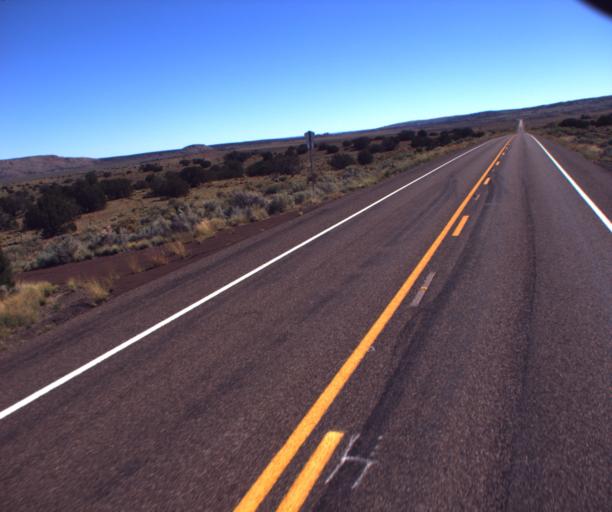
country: US
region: Arizona
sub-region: Apache County
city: Saint Johns
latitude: 34.5951
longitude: -109.6224
